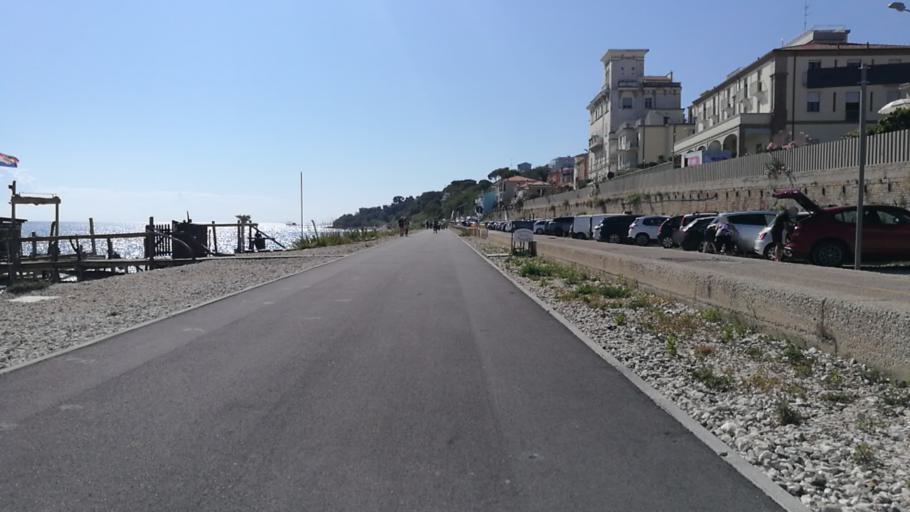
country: IT
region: Abruzzo
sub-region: Provincia di Chieti
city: Marina di San Vito
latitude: 42.3059
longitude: 14.4503
